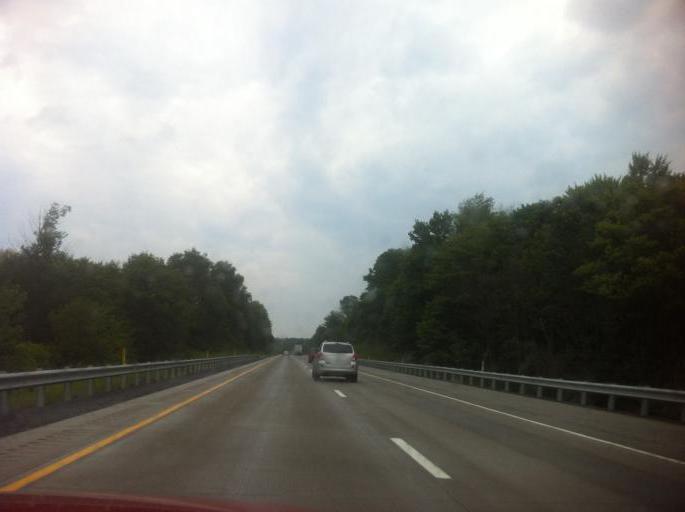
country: US
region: Pennsylvania
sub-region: Jefferson County
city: Falls Creek
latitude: 41.1550
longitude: -78.8124
